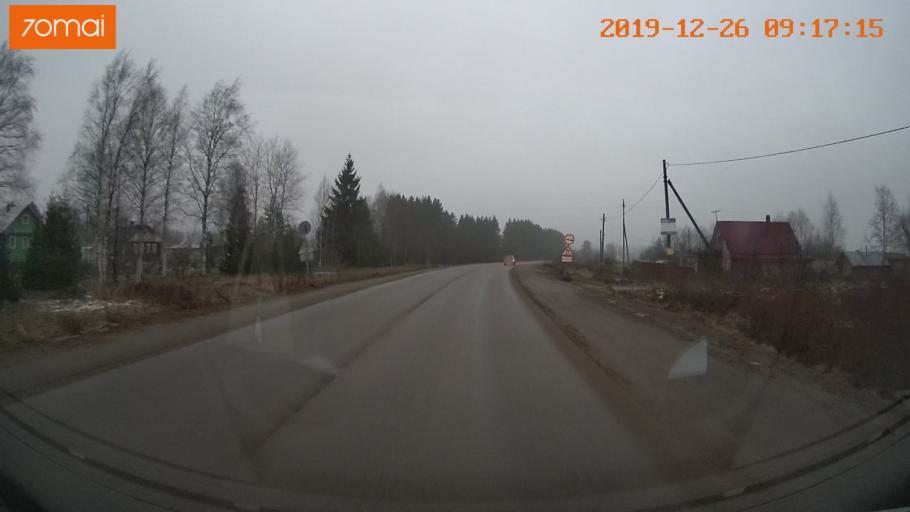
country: RU
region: Vologda
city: Gryazovets
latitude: 58.9276
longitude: 40.2385
